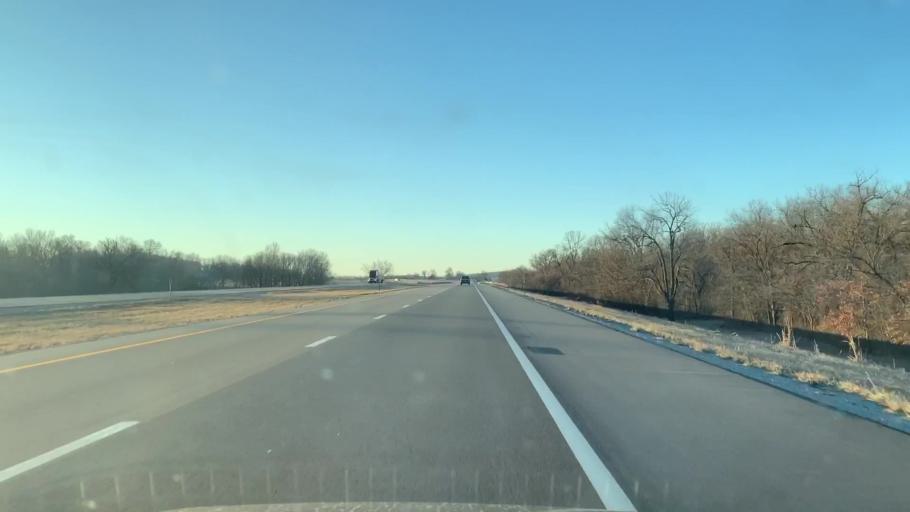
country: US
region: Kansas
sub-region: Linn County
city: La Cygne
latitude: 38.3031
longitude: -94.6776
